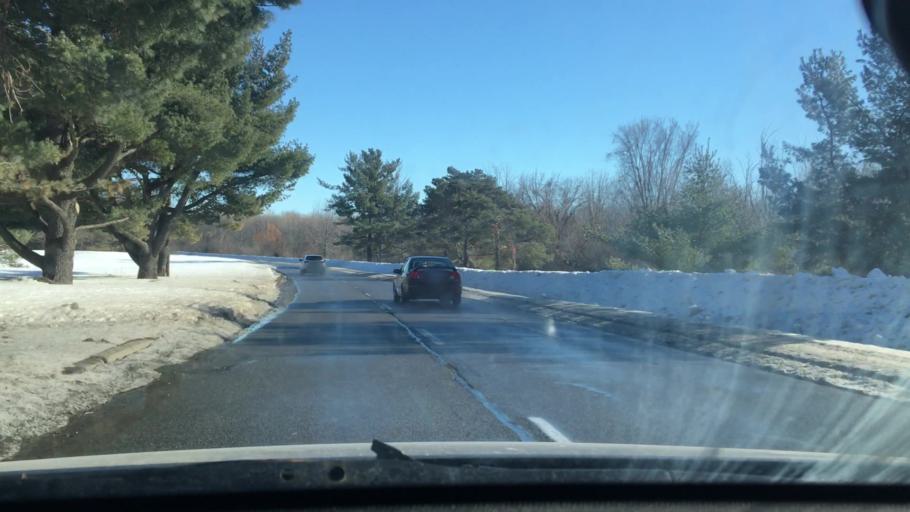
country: CA
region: Ontario
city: Ottawa
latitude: 45.4331
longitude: -75.6332
